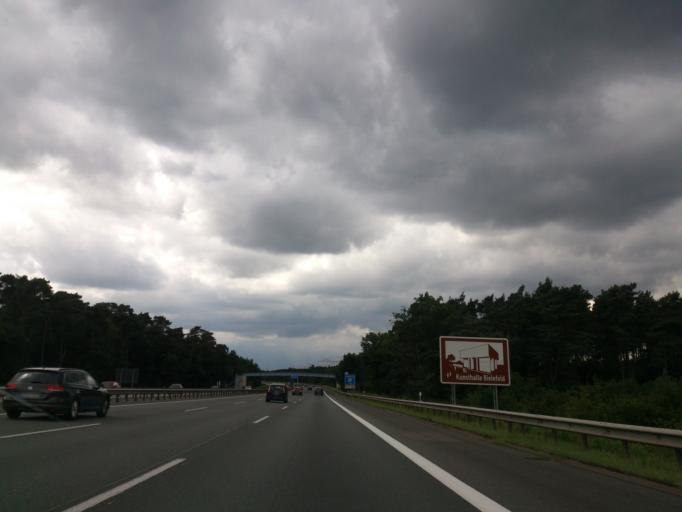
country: DE
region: North Rhine-Westphalia
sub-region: Regierungsbezirk Detmold
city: Oerlinghausen
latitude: 51.9633
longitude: 8.5896
